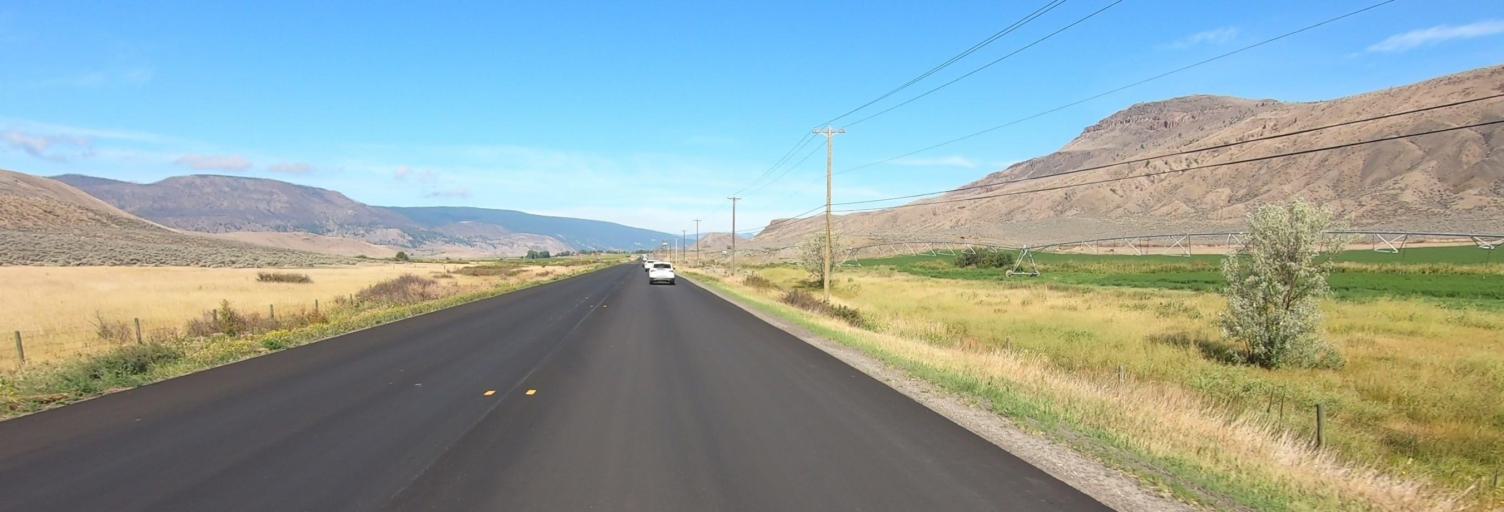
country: CA
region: British Columbia
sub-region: Thompson-Nicola Regional District
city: Ashcroft
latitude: 50.7935
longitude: -121.2447
